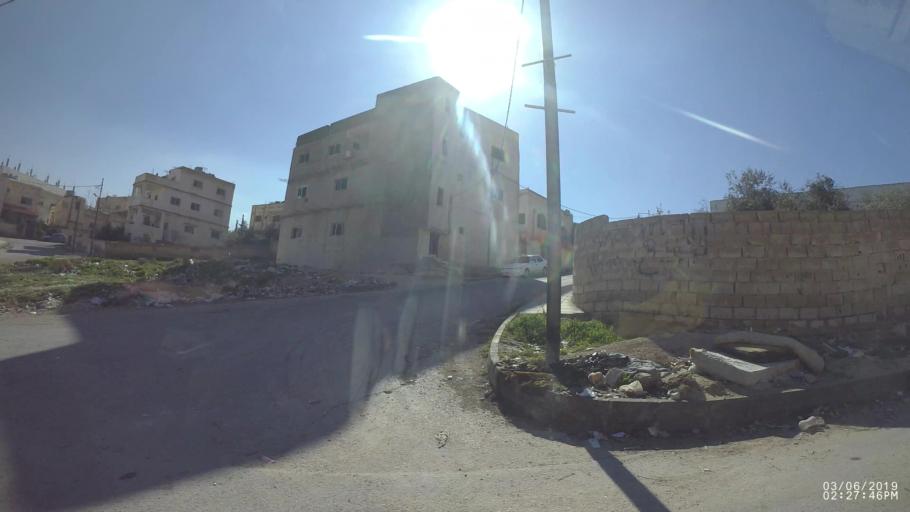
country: JO
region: Zarqa
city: Russeifa
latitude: 32.0368
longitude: 36.0329
